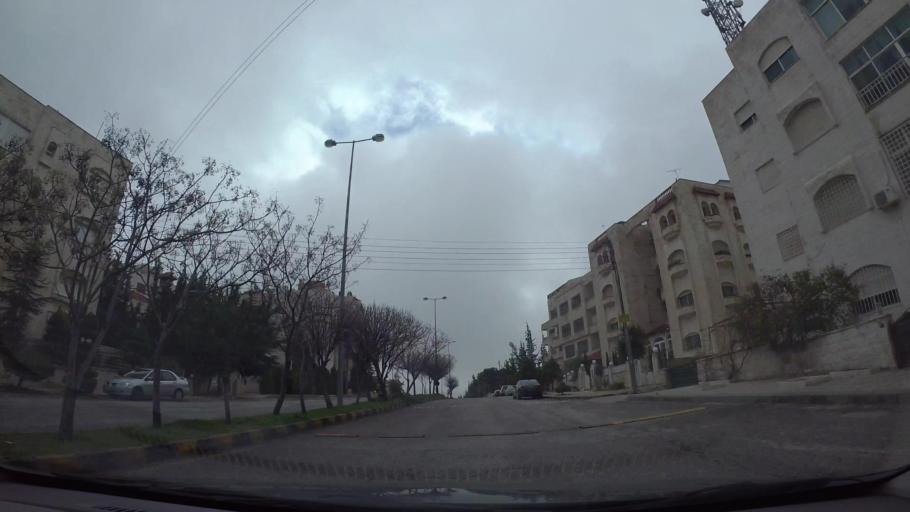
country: JO
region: Amman
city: Wadi as Sir
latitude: 31.9408
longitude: 35.8623
